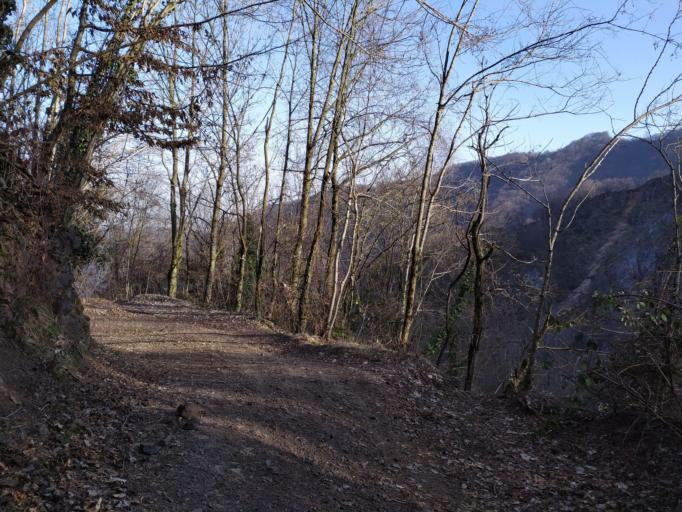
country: IT
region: Veneto
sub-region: Provincia di Vicenza
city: San Quirico
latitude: 45.6986
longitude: 11.2870
